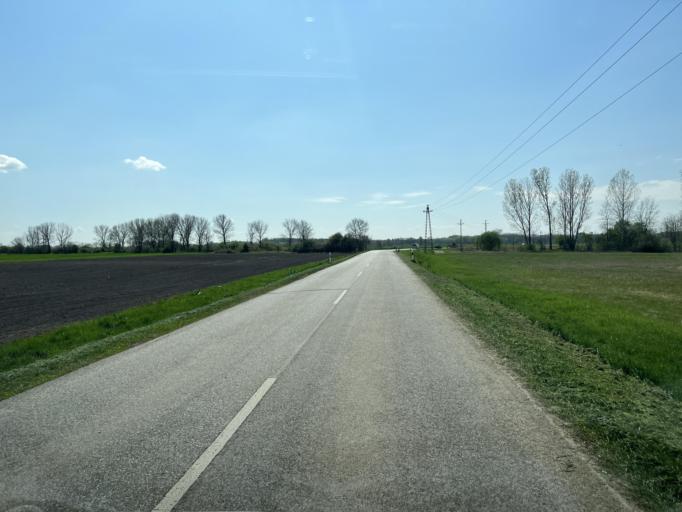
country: HU
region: Pest
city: Inarcs
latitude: 47.2298
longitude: 19.3047
